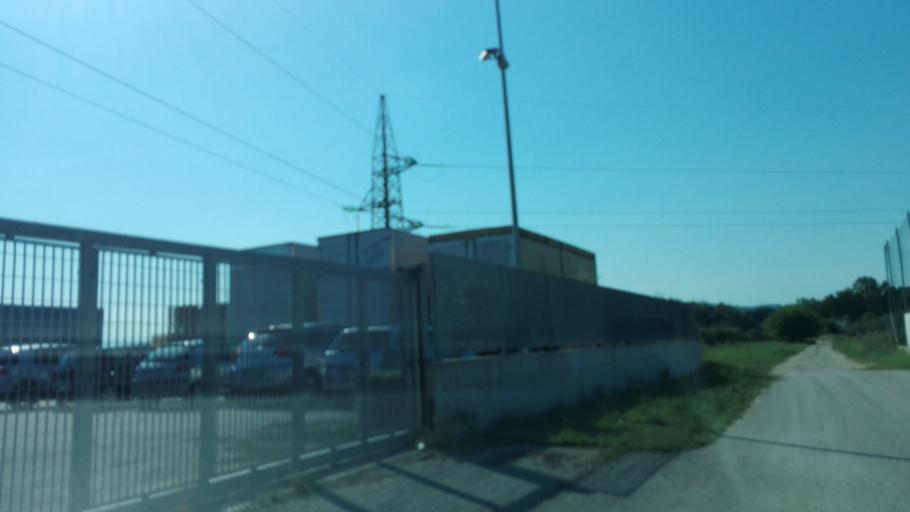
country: IT
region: Abruzzo
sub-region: Provincia di Pescara
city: Cappelle sul Tavo
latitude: 42.4876
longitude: 14.1171
